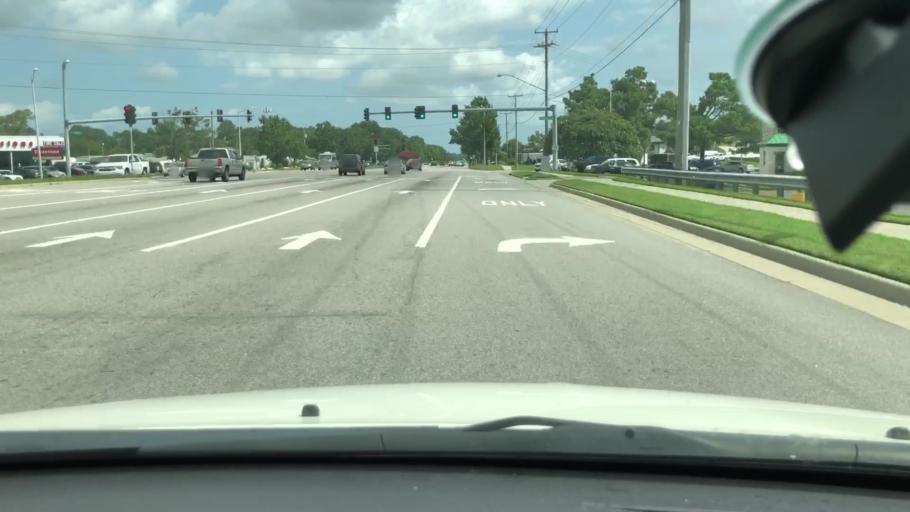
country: US
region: Virginia
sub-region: City of Chesapeake
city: Chesapeake
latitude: 36.8104
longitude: -76.2183
